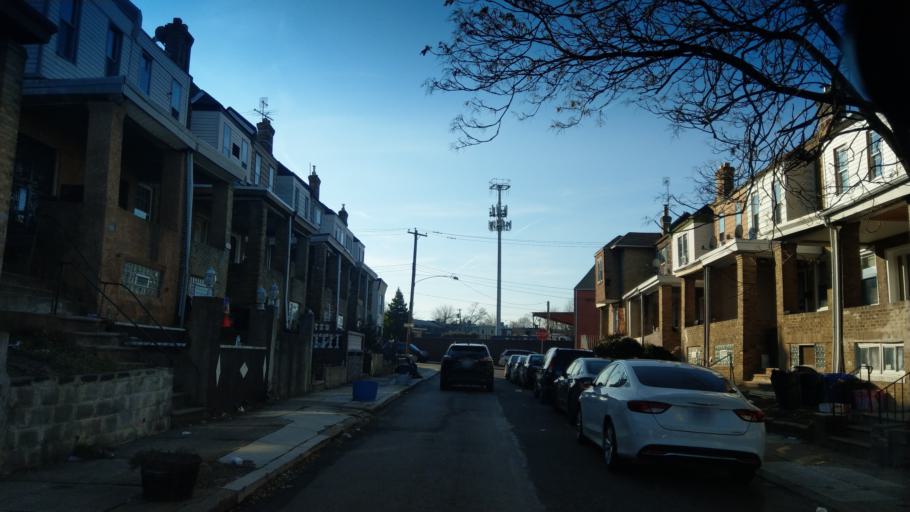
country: US
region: Pennsylvania
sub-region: Montgomery County
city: Rockledge
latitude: 40.0268
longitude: -75.1253
